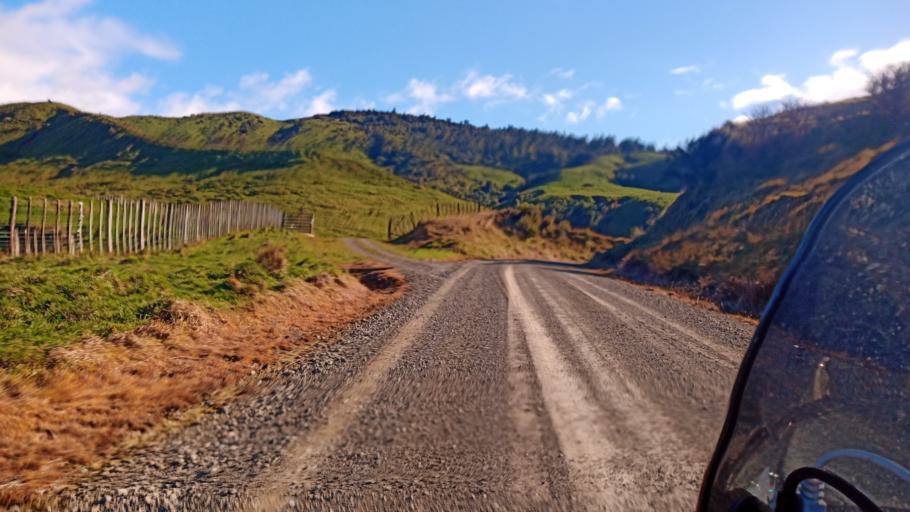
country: NZ
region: Hawke's Bay
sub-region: Wairoa District
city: Wairoa
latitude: -38.7574
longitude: 177.2645
